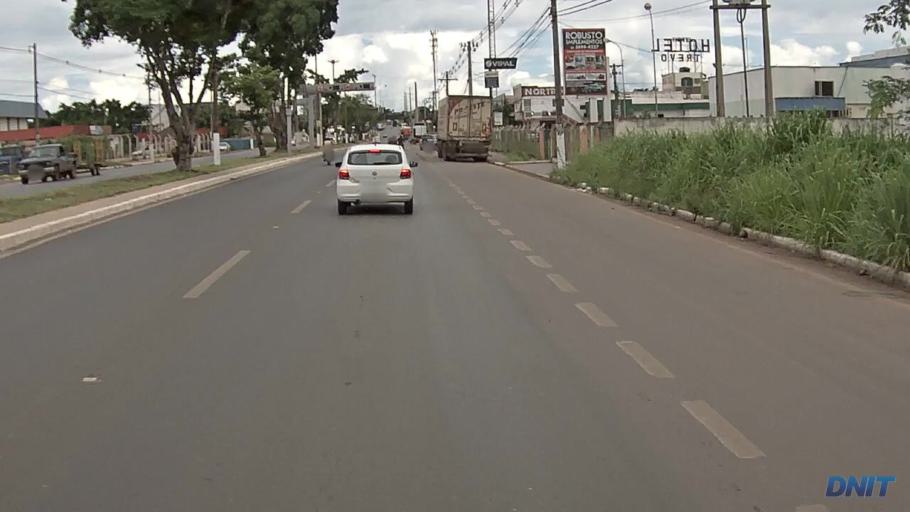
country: BR
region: Mato Grosso
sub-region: Varzea Grande
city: Varzea Grande
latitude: -15.6458
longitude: -56.1868
